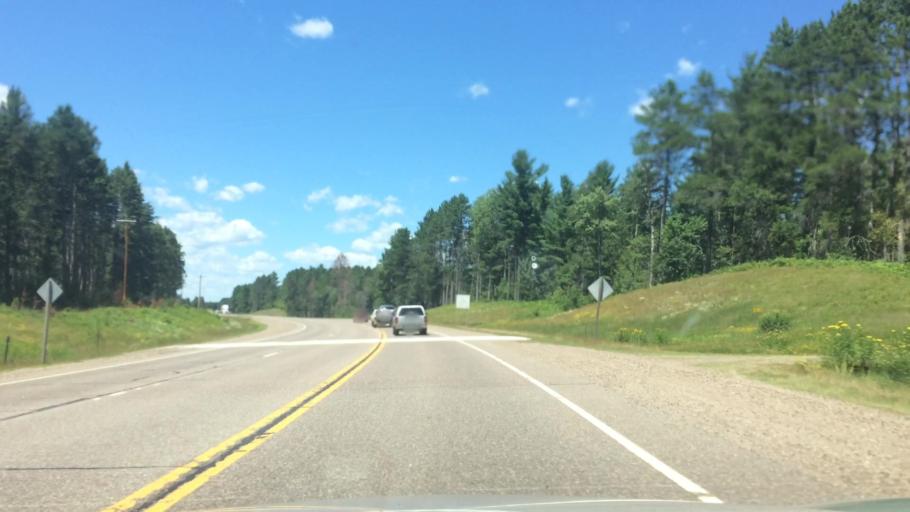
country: US
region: Wisconsin
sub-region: Lincoln County
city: Tomahawk
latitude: 45.6572
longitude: -89.7055
